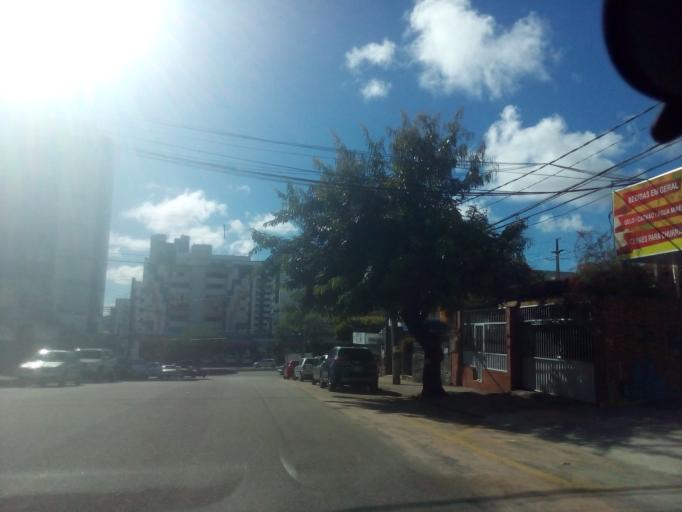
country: BR
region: Rio Grande do Norte
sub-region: Natal
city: Natal
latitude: -5.8023
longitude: -35.2055
